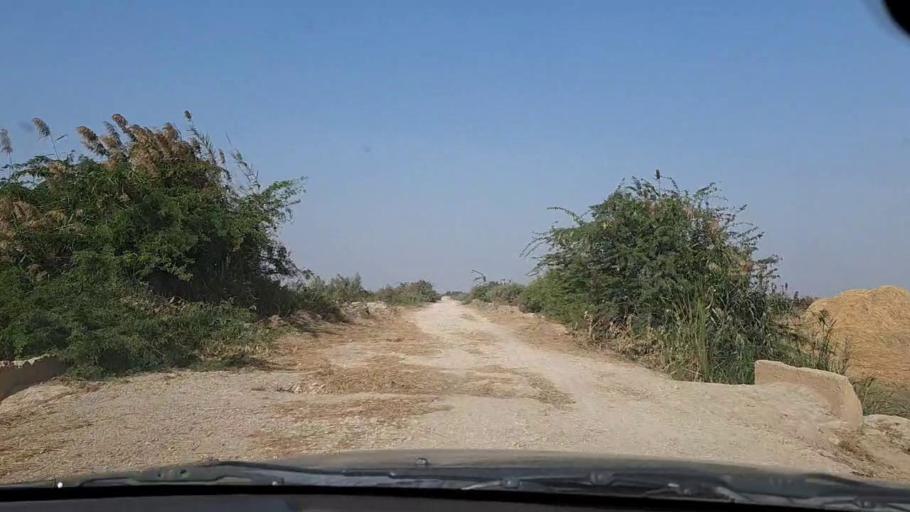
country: PK
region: Sindh
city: Mirpur Sakro
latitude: 24.3522
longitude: 67.6831
